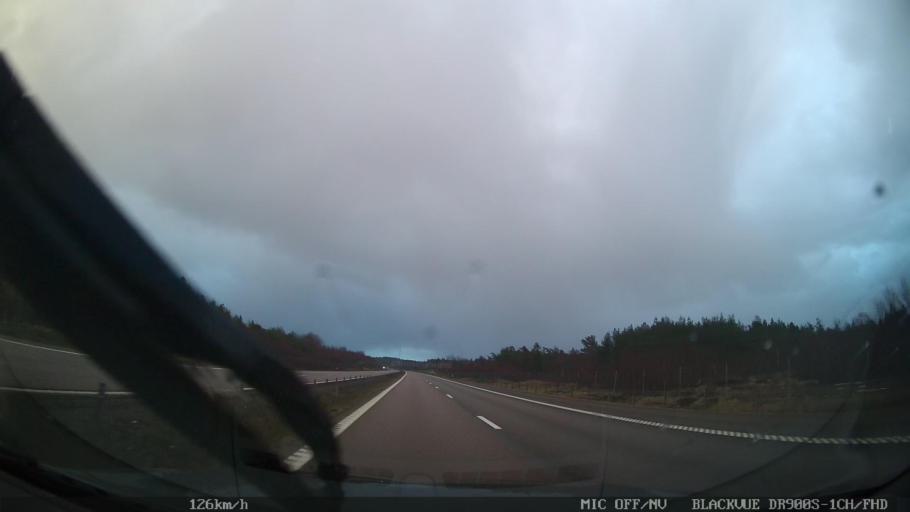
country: SE
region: Skane
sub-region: Orkelljunga Kommun
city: OErkelljunga
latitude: 56.2590
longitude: 13.2647
